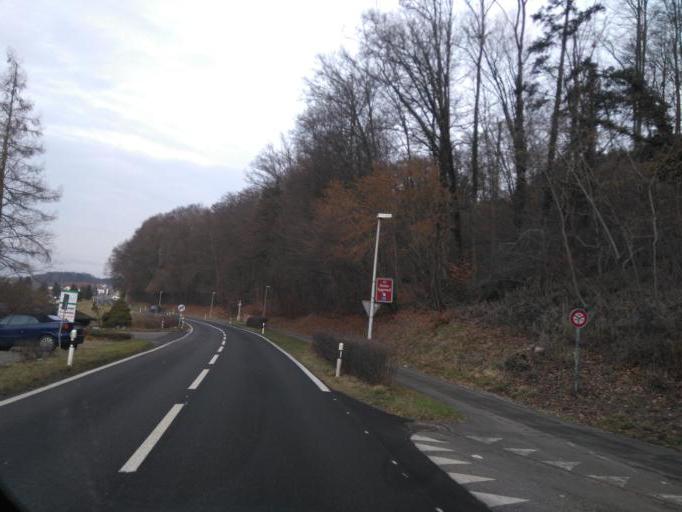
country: CH
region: Aargau
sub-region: Bezirk Bremgarten
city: Bremgarten
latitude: 47.3626
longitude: 8.3454
